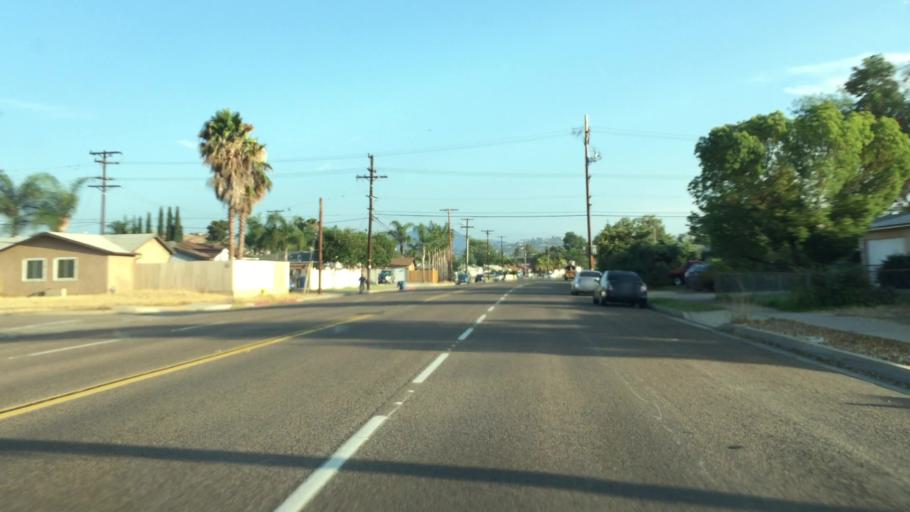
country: US
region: California
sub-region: San Diego County
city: Bostonia
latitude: 32.8176
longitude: -116.9497
